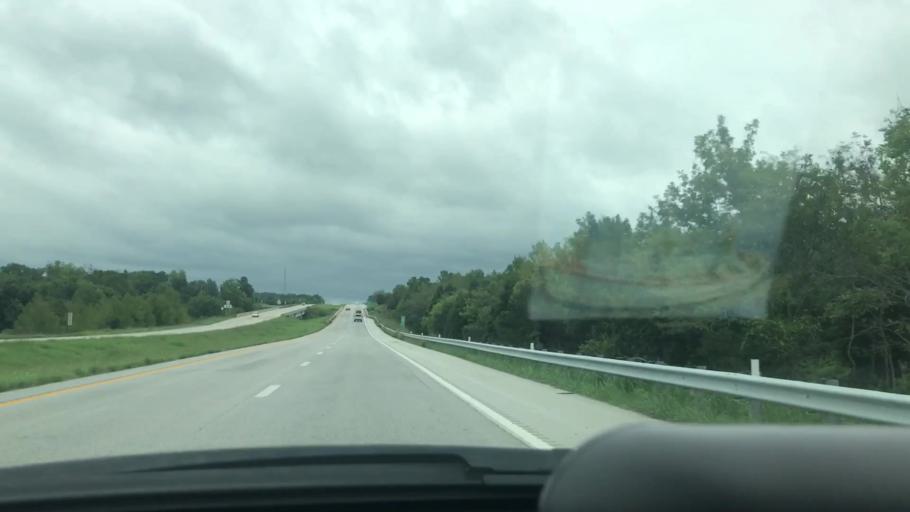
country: US
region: Missouri
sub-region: Greene County
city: Fair Grove
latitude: 37.4130
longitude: -93.1452
